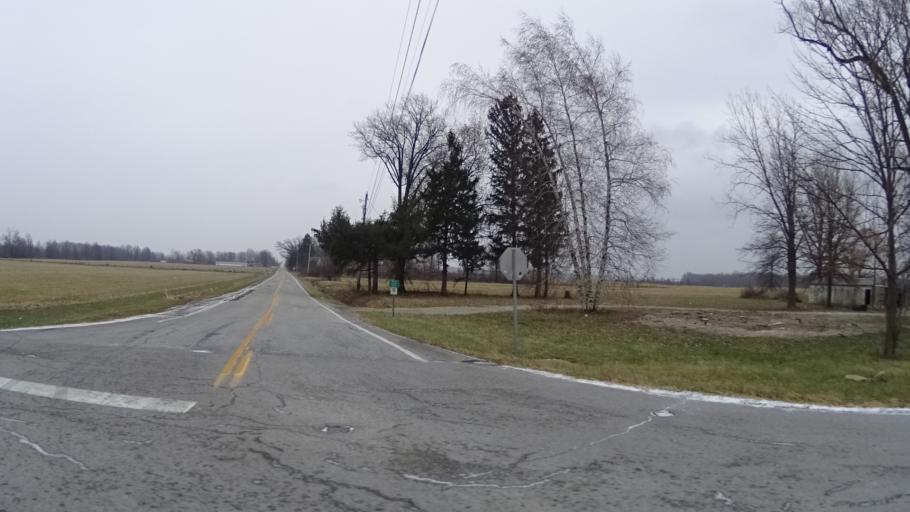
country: US
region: Ohio
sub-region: Lorain County
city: Amherst
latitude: 41.3525
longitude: -82.1942
